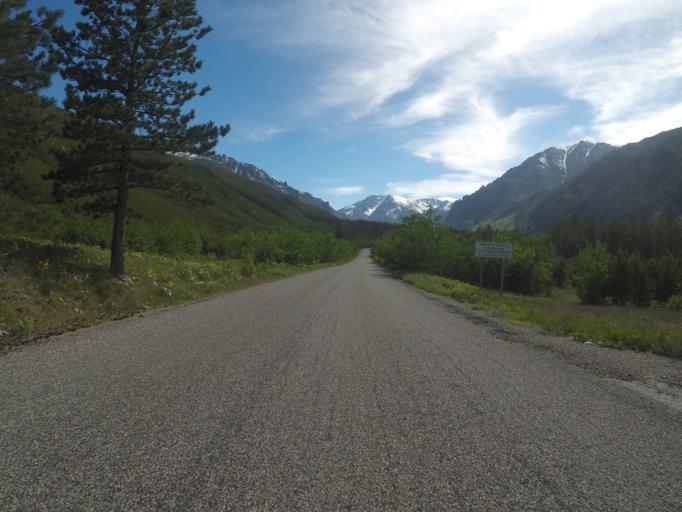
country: US
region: Montana
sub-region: Stillwater County
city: Absarokee
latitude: 45.2490
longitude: -109.5746
